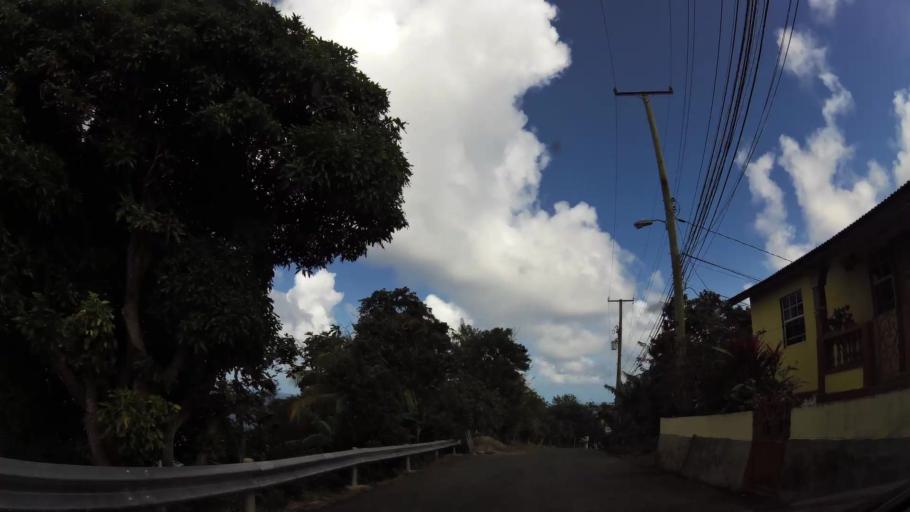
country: DM
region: Saint John
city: Portsmouth
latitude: 15.6183
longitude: -61.4107
